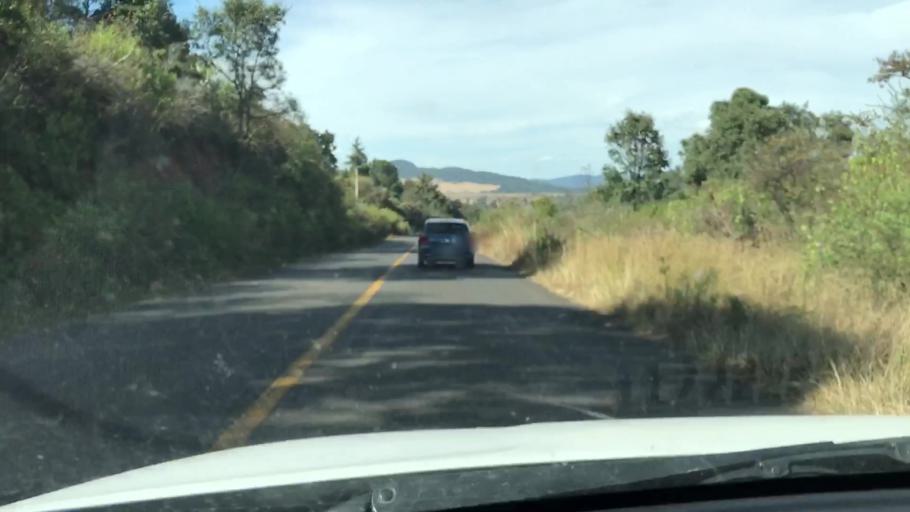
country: MX
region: Jalisco
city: Chiquilistlan
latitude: 20.1440
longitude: -103.7225
